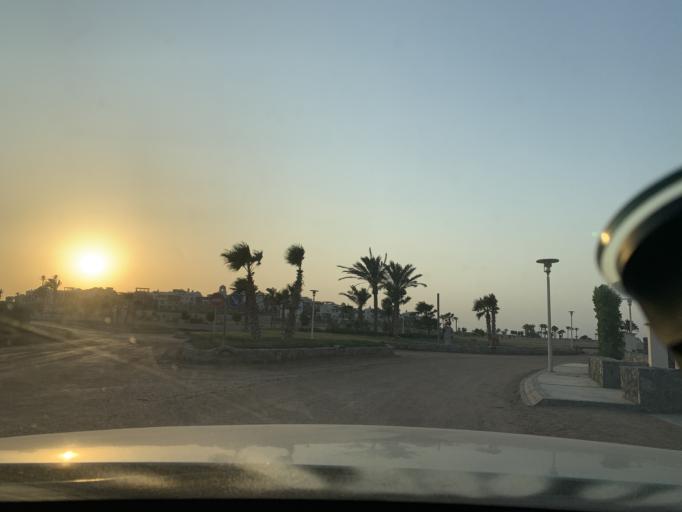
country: EG
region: Red Sea
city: El Gouna
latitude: 27.4107
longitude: 33.6663
